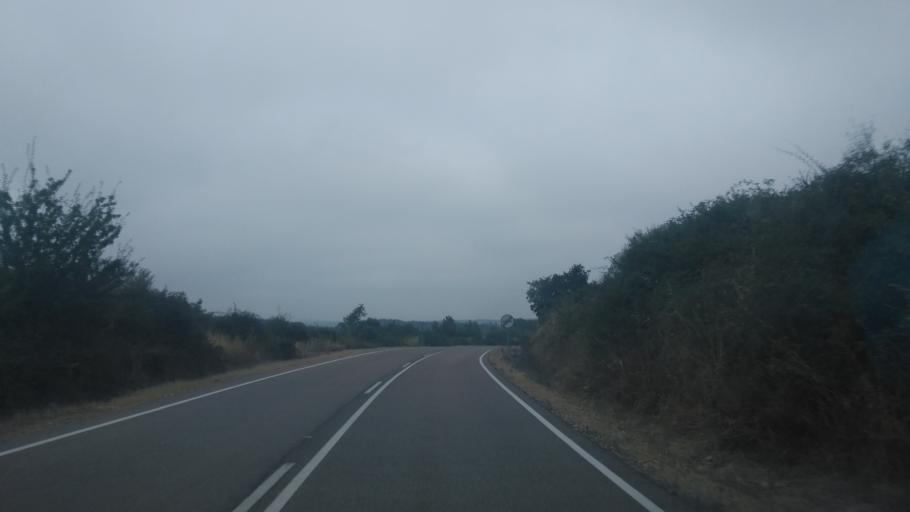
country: ES
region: Castille and Leon
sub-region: Provincia de Salamanca
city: Cereceda de la Sierra
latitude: 40.5624
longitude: -6.0858
